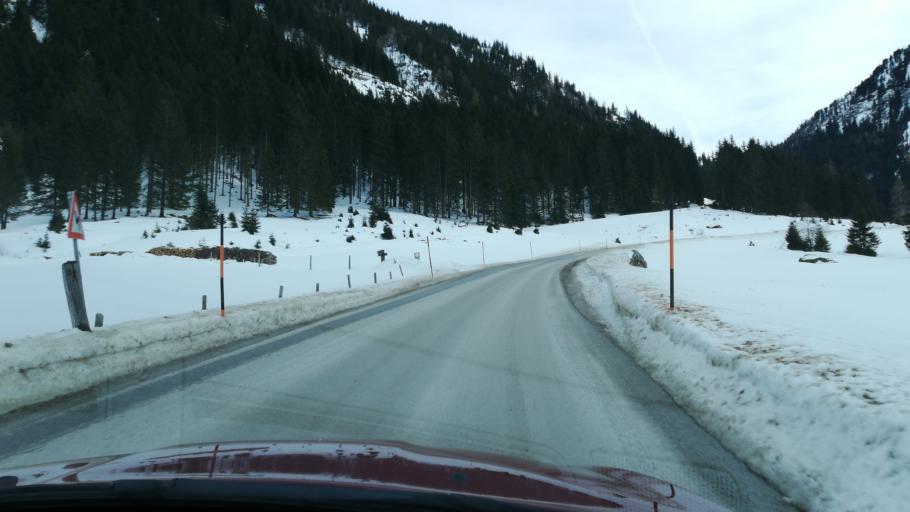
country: AT
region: Styria
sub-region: Politischer Bezirk Liezen
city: Donnersbach
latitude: 47.4176
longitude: 14.1737
